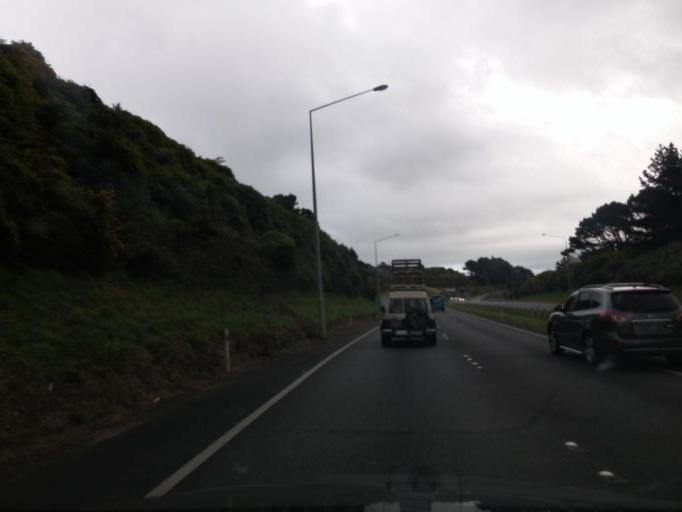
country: NZ
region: Wellington
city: Petone
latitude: -41.2006
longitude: 174.8238
